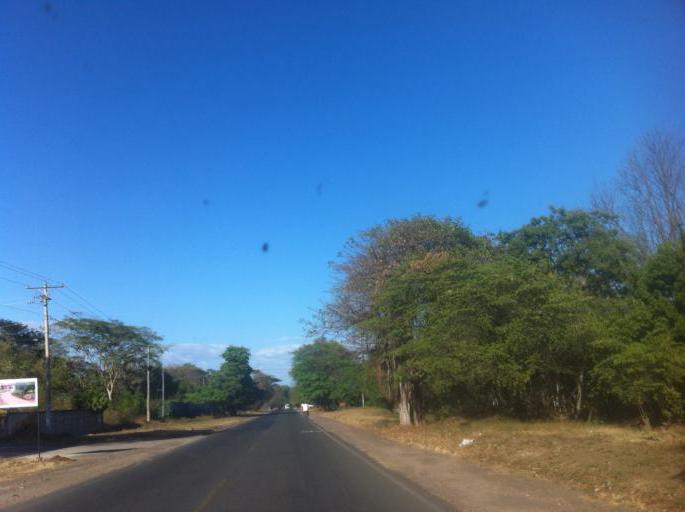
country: NI
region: Granada
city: Granada
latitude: 11.9067
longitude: -85.9814
